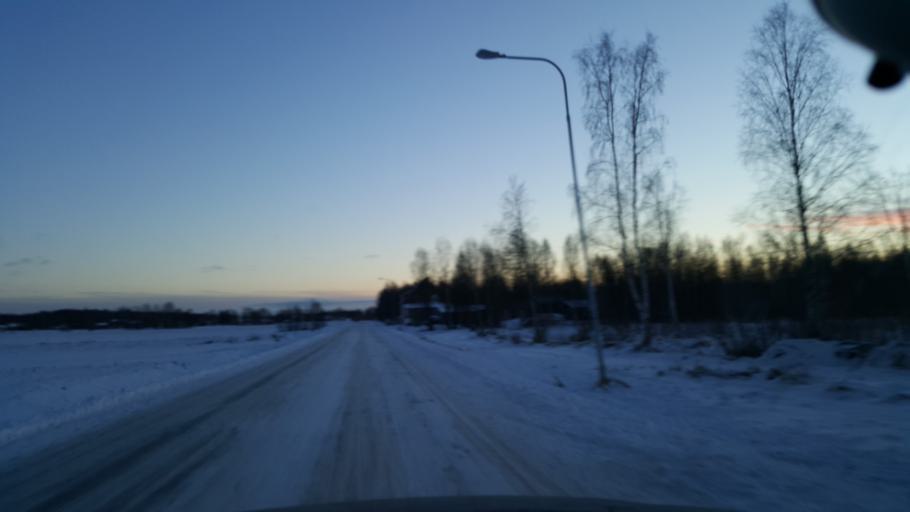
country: SE
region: Norrbotten
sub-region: Lulea Kommun
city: Sodra Sunderbyn
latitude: 65.5394
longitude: 21.9031
